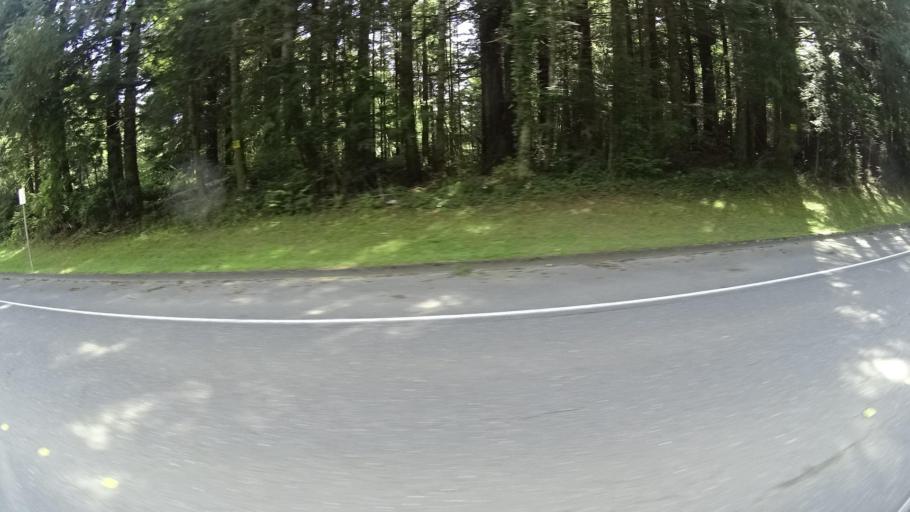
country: US
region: California
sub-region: Humboldt County
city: Cutten
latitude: 40.7555
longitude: -124.1470
